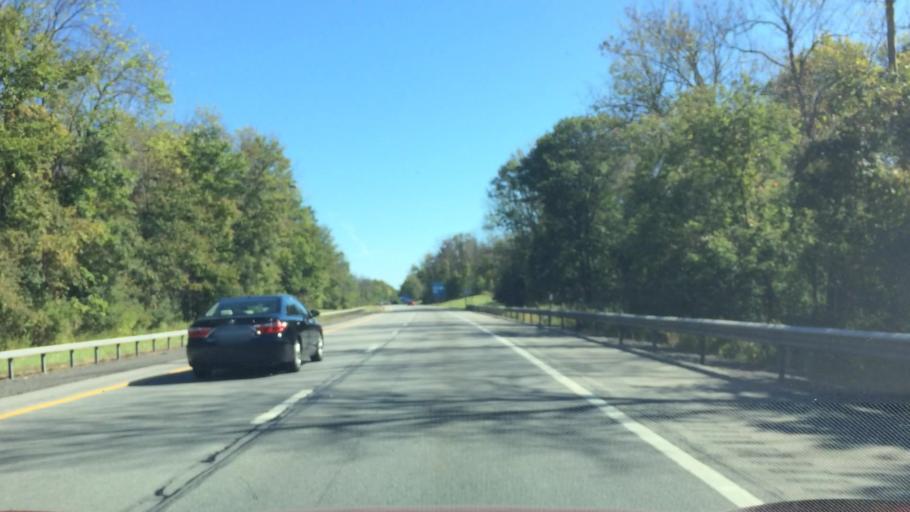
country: US
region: New York
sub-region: Ontario County
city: Shortsville
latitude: 42.9748
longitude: -77.2021
